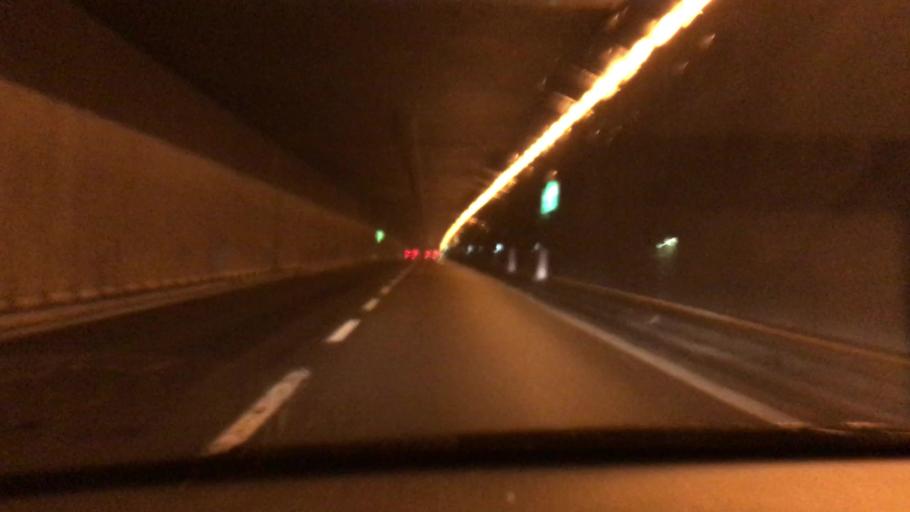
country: IT
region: Lombardy
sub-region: Provincia di Lecco
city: Colico Piano
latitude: 46.1315
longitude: 9.3796
